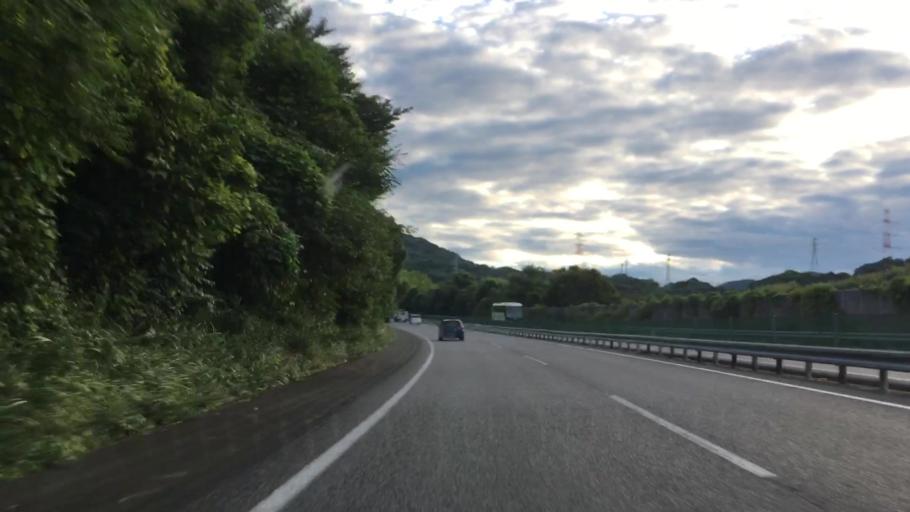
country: JP
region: Yamaguchi
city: Shimonoseki
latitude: 34.0443
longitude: 130.9887
